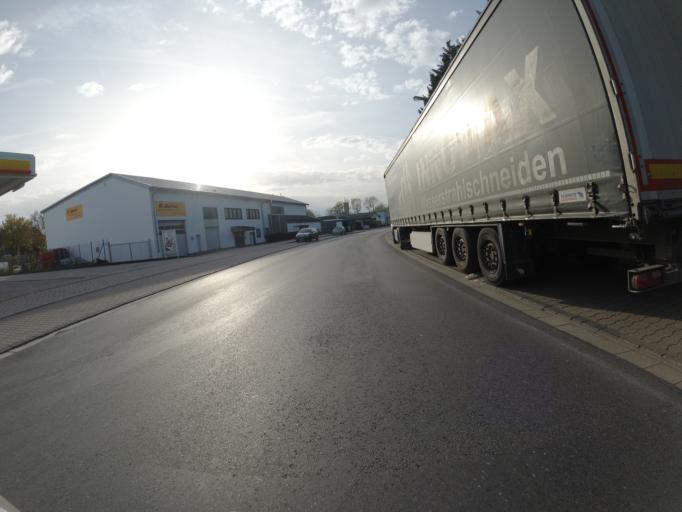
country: DE
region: North Rhine-Westphalia
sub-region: Regierungsbezirk Dusseldorf
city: Moers
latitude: 51.4579
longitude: 6.6095
